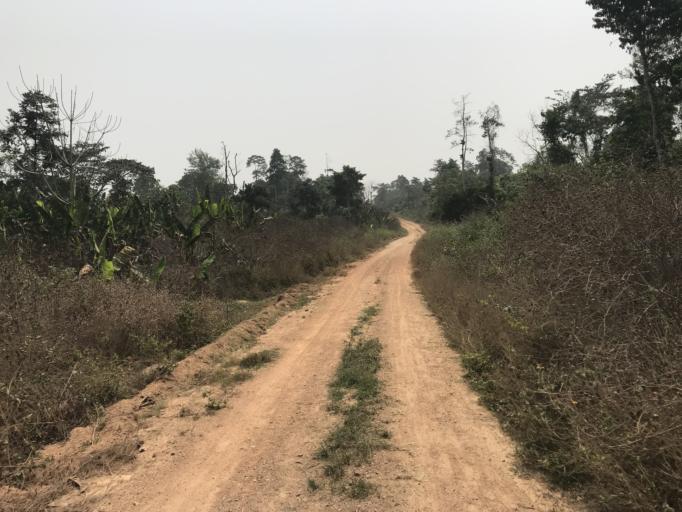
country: NG
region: Osun
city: Ifetedo
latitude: 7.0347
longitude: 4.4754
